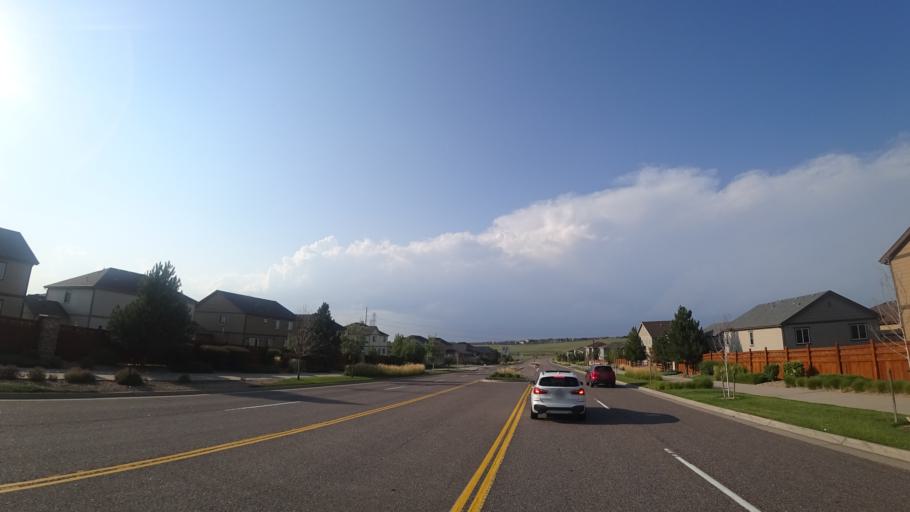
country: US
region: Colorado
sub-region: Arapahoe County
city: Dove Valley
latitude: 39.6282
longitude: -104.7382
